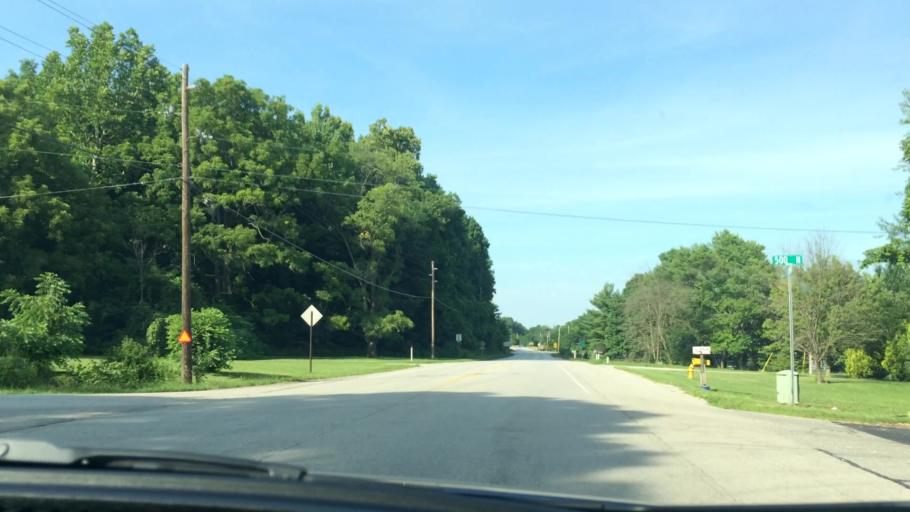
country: US
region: Indiana
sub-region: Tippecanoe County
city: Battle Ground
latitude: 40.4878
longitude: -86.8749
